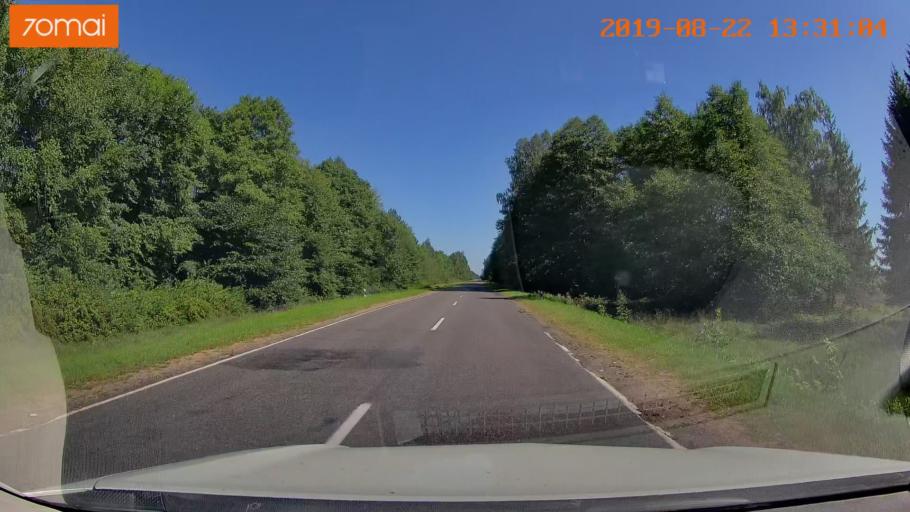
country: BY
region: Minsk
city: Staryya Darohi
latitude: 53.2173
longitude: 28.1701
